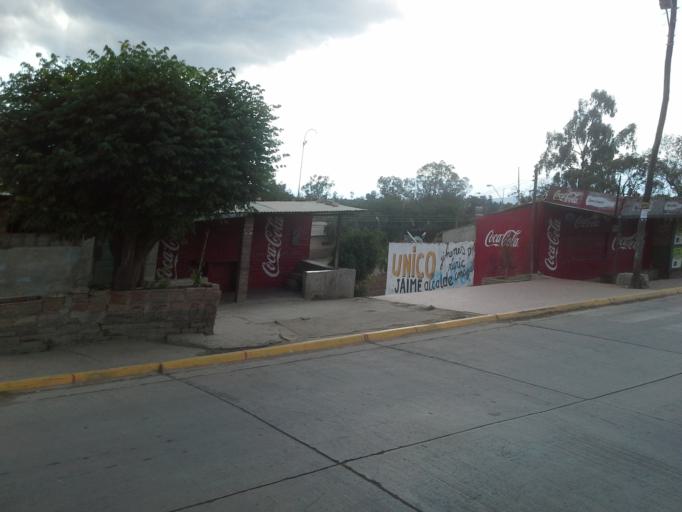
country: BO
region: Cochabamba
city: Cochabamba
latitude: -17.4599
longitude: -66.1235
